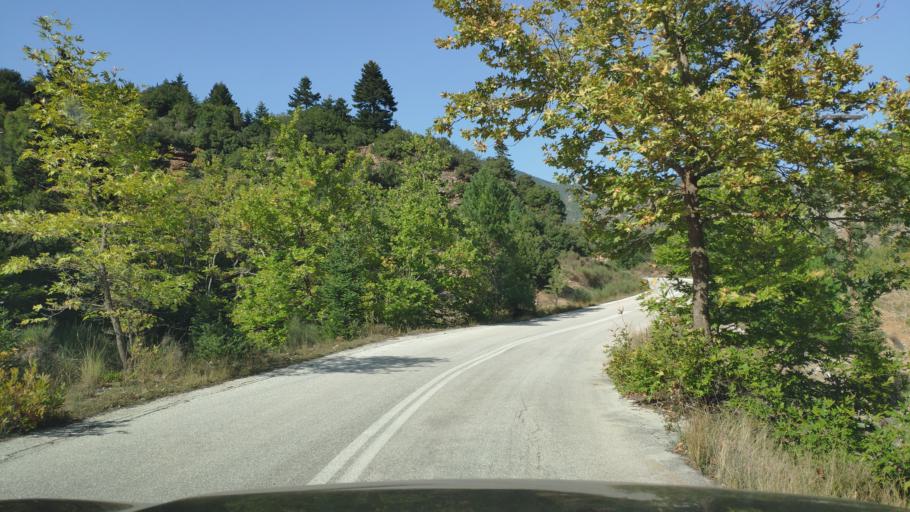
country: GR
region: West Greece
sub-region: Nomos Achaias
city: Aiyira
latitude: 37.9768
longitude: 22.3539
